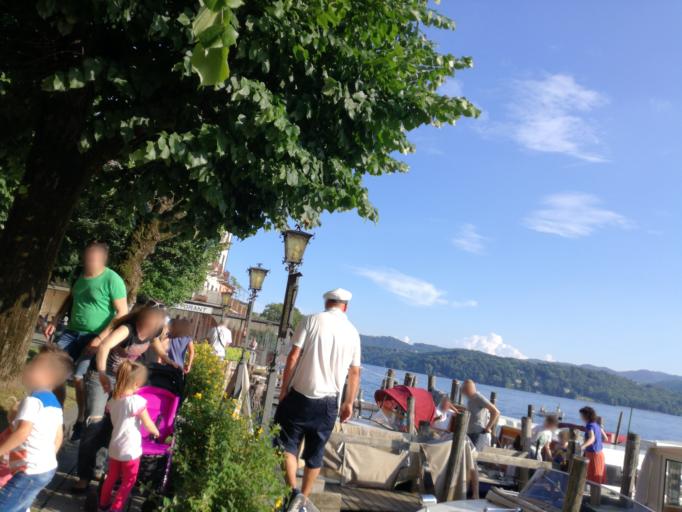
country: IT
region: Piedmont
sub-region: Provincia di Novara
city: Orta San Giulio
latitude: 45.7979
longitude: 8.4057
